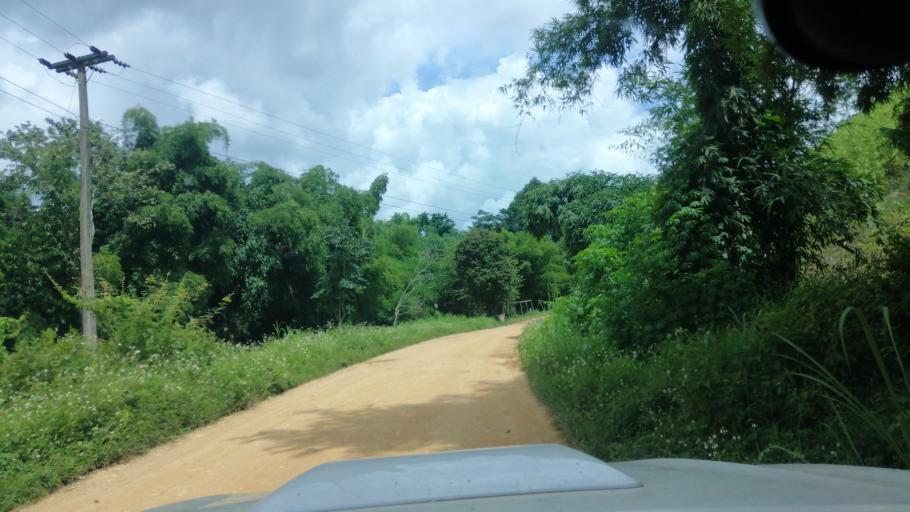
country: TH
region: Phayao
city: Phu Sang
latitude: 19.6795
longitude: 100.5033
